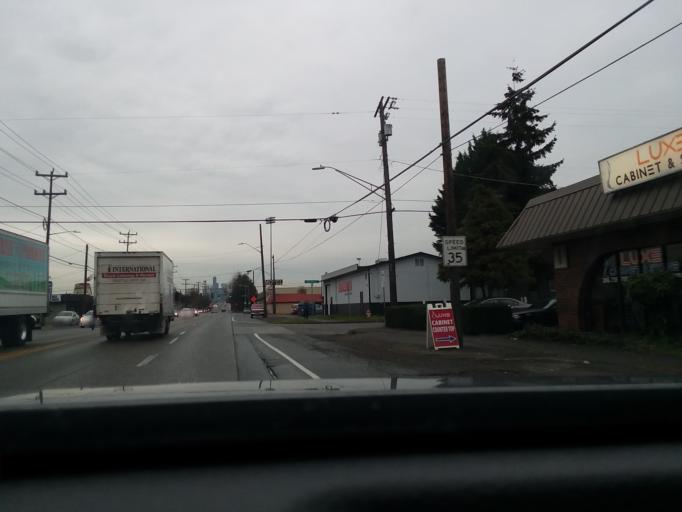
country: US
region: Washington
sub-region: King County
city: White Center
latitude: 47.5538
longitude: -122.3295
